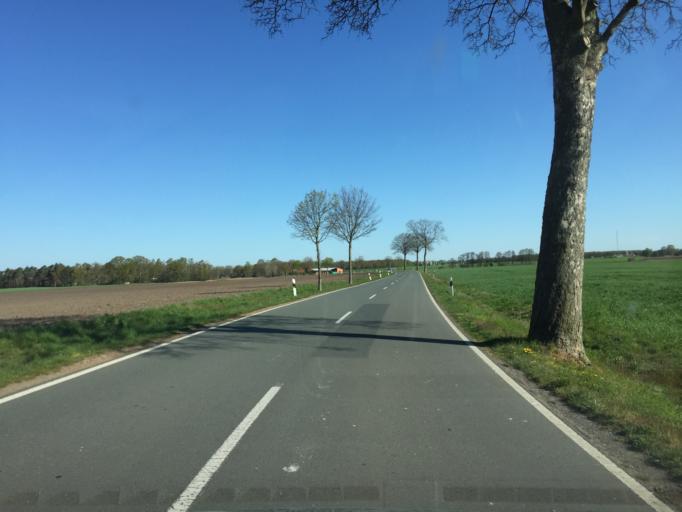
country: DE
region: Lower Saxony
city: Varrel
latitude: 52.6329
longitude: 8.7377
